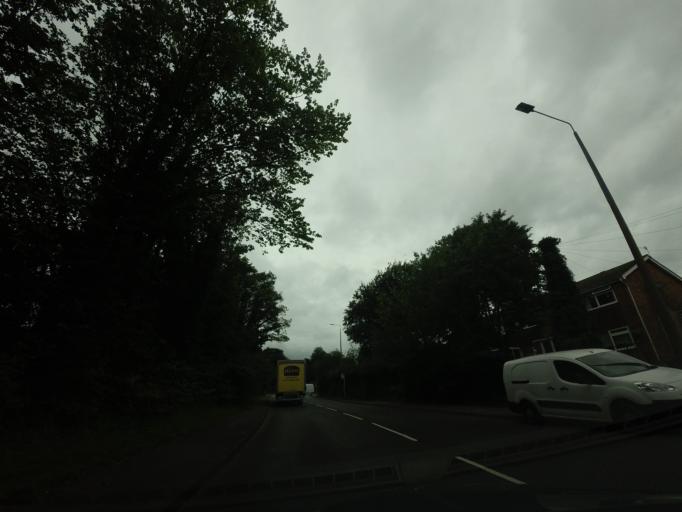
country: GB
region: England
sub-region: Nottinghamshire
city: Kimberley
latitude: 52.9973
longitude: -1.2359
